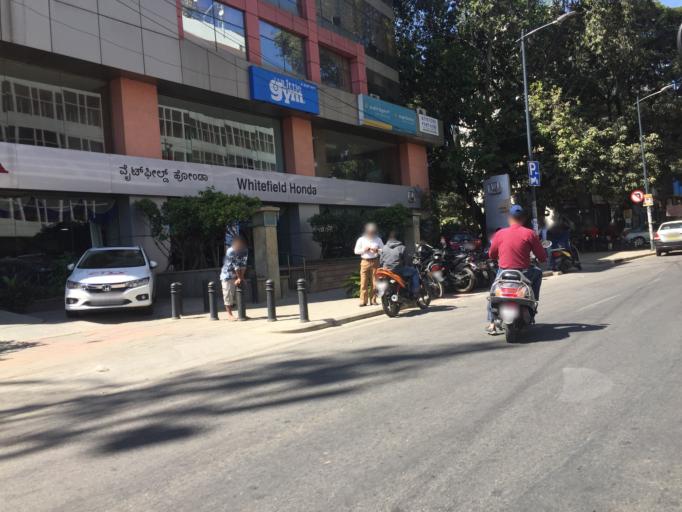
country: IN
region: Karnataka
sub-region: Bangalore Urban
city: Bangalore
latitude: 12.9864
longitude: 77.5953
